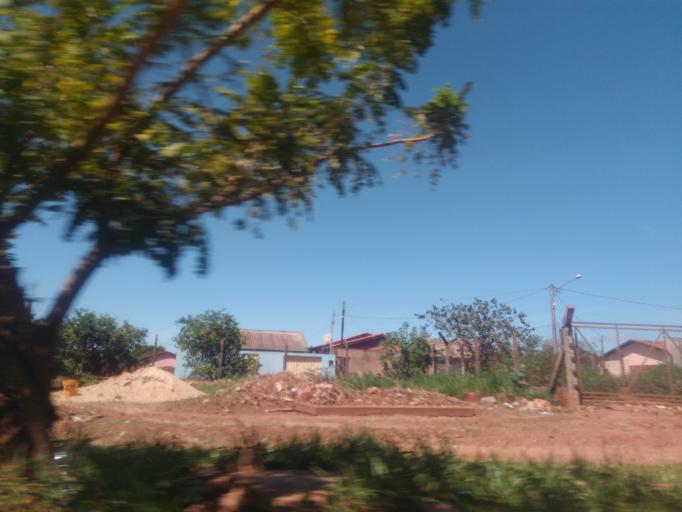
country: BR
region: Mato Grosso do Sul
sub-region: Ponta Pora
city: Ponta Pora
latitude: -22.5063
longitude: -55.7276
